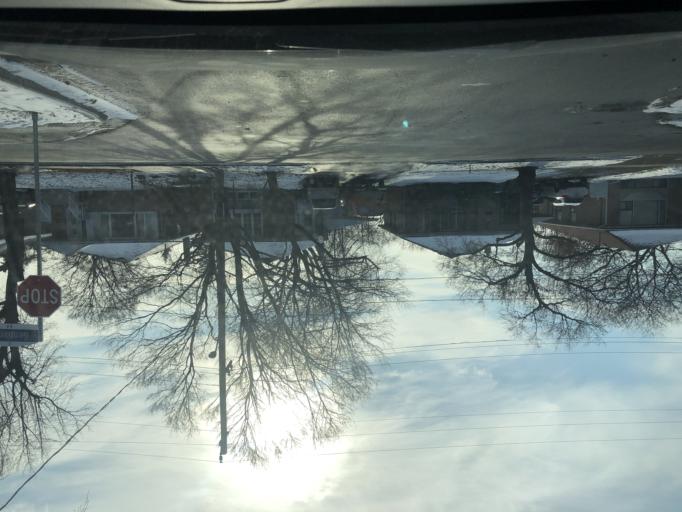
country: CA
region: Ontario
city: Etobicoke
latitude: 43.6654
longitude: -79.5849
